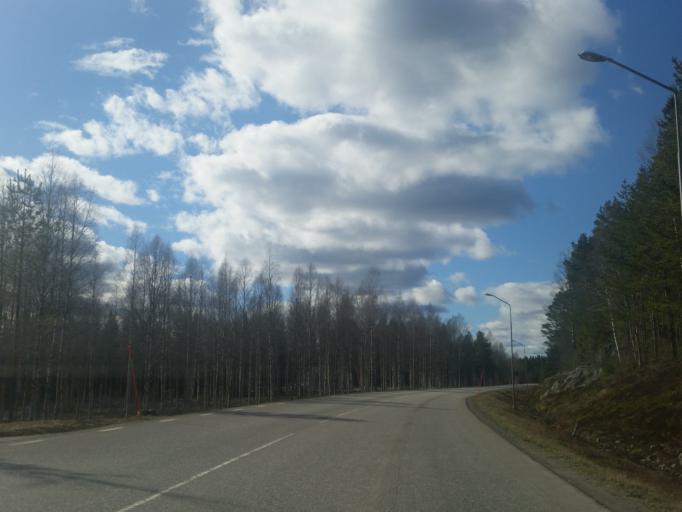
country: SE
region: Vaesterbotten
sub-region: Robertsfors Kommun
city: Robertsfors
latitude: 64.1975
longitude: 20.8375
